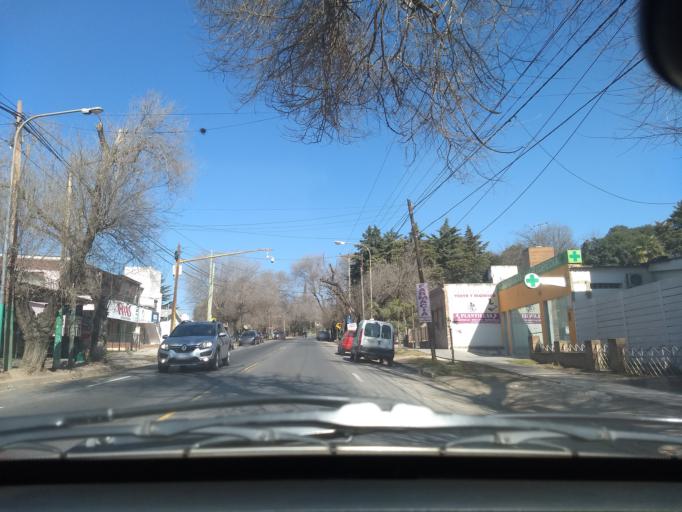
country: AR
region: Cordoba
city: Salsipuedes
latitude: -31.1402
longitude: -64.2969
